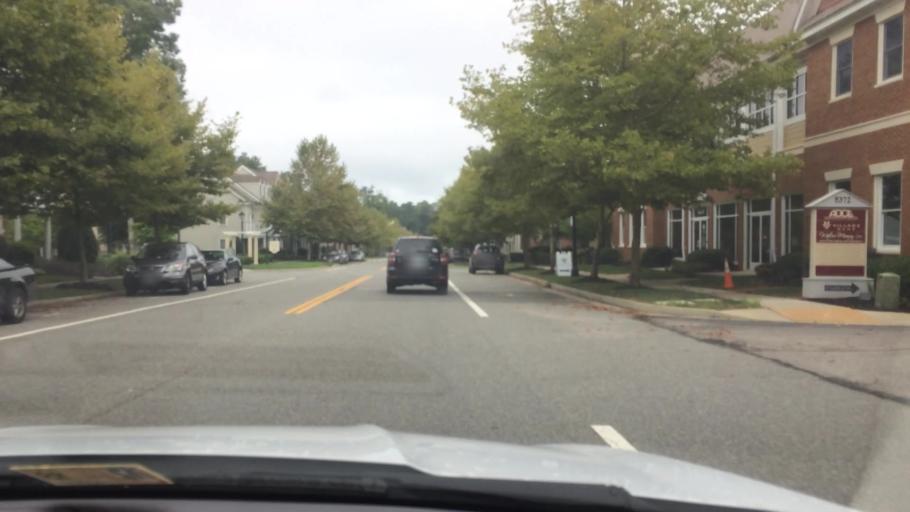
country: US
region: Virginia
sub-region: James City County
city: Williamsburg
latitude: 37.2817
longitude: -76.7410
